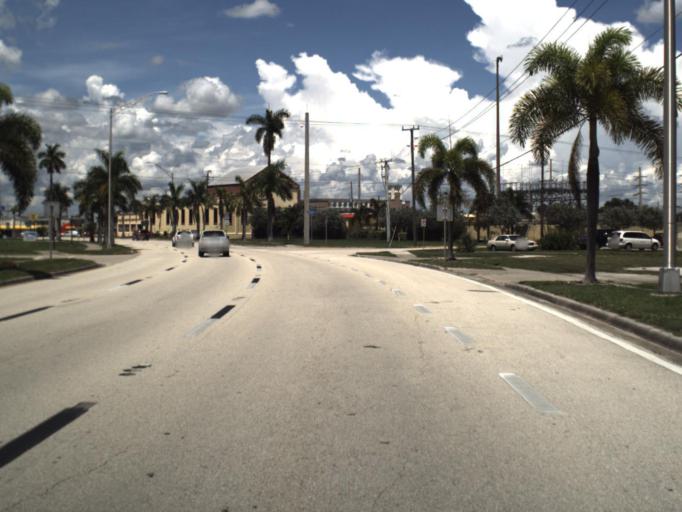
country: US
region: Florida
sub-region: Charlotte County
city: Punta Gorda
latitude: 26.9323
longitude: -82.0472
